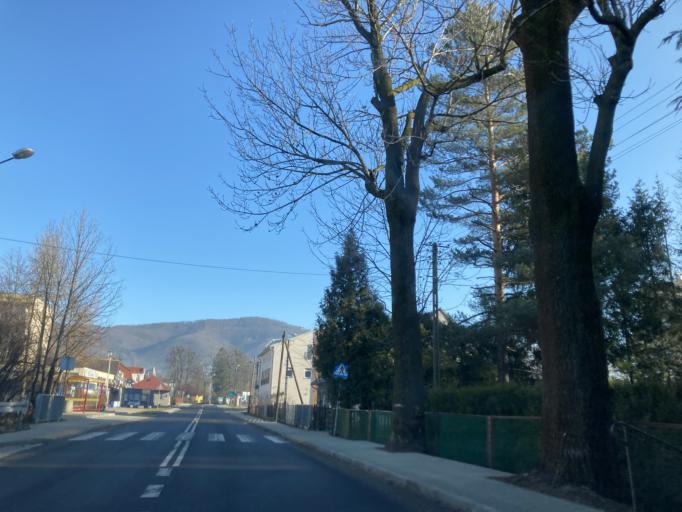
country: PL
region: Silesian Voivodeship
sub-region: Powiat cieszynski
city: Ustron
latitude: 49.7221
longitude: 18.8055
